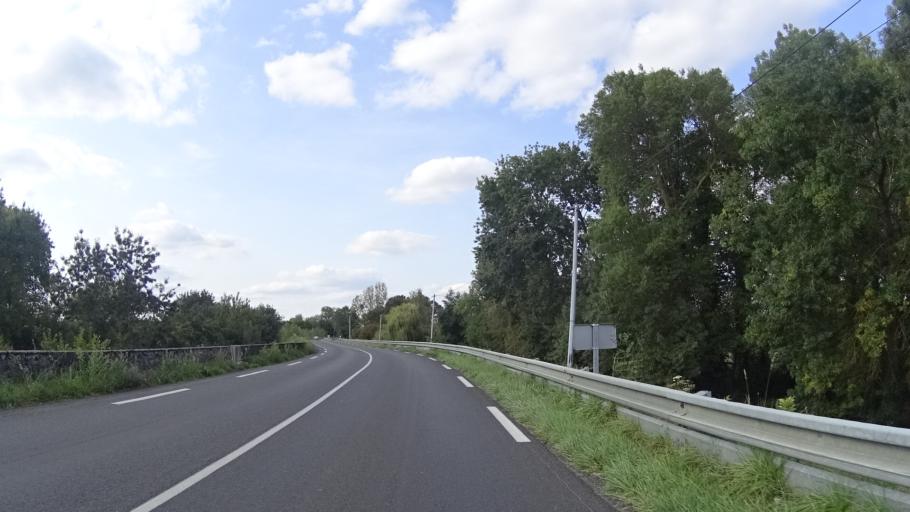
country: FR
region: Pays de la Loire
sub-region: Departement de Maine-et-Loire
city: Gennes
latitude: 47.3568
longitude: -0.2419
